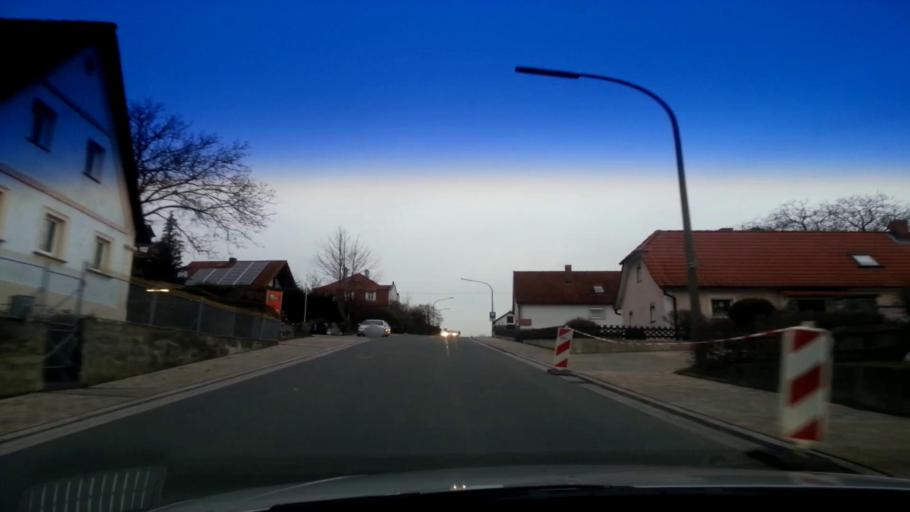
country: DE
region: Bavaria
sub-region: Upper Franconia
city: Litzendorf
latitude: 49.9130
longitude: 11.0092
